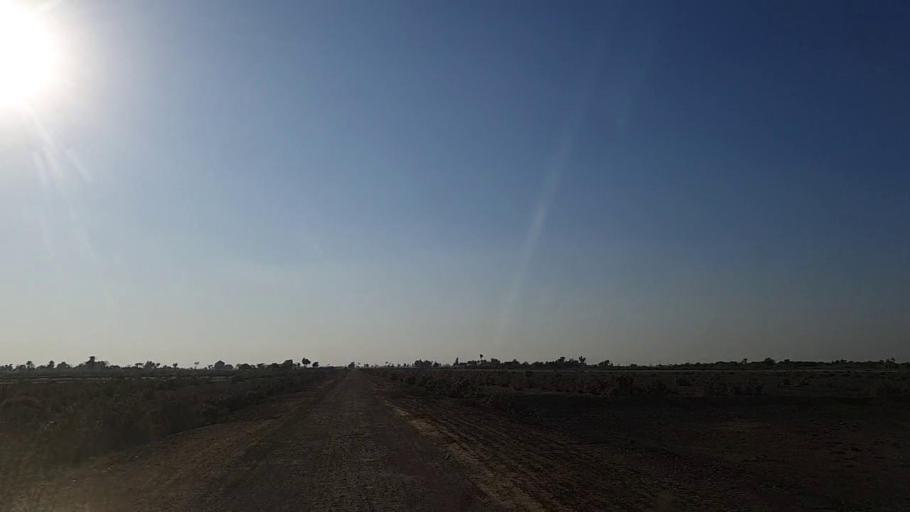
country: PK
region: Sindh
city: Samaro
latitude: 25.3442
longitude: 69.3748
